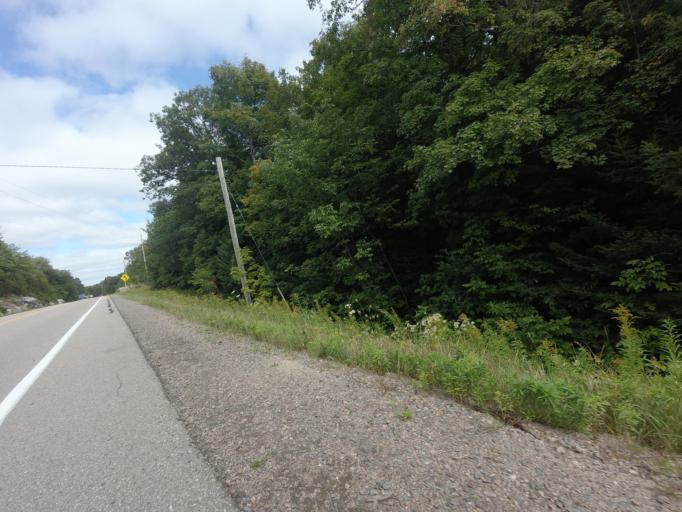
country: CA
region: Ontario
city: Bancroft
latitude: 44.9428
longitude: -78.2989
